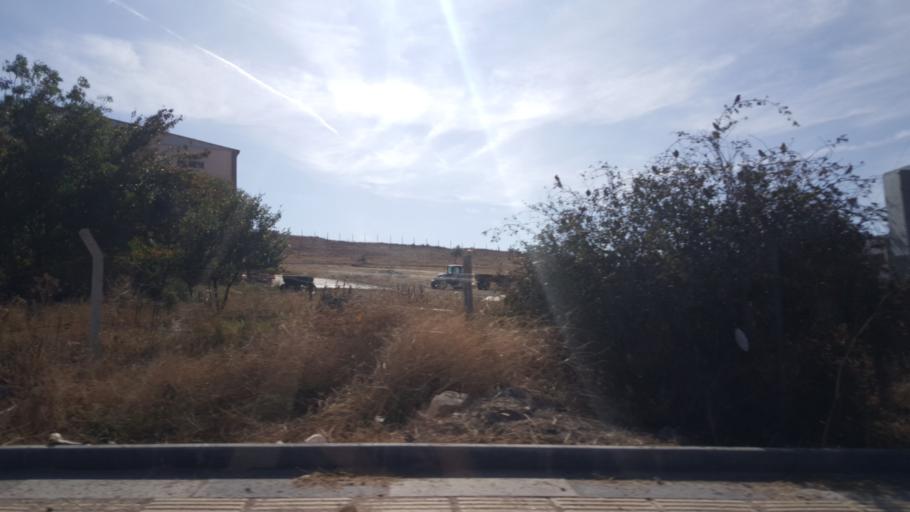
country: TR
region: Ankara
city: Haymana
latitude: 39.4294
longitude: 32.5223
